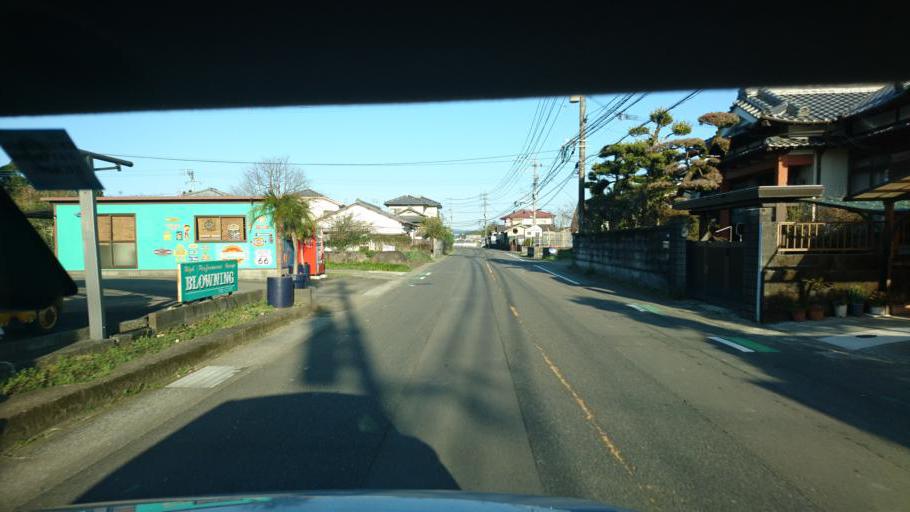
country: JP
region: Miyazaki
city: Miyazaki-shi
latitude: 31.8446
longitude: 131.3982
